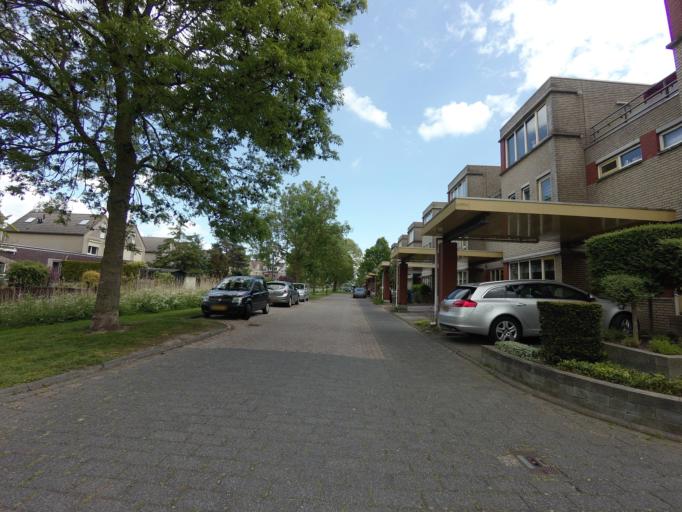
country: NL
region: North Brabant
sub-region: Gemeente Woudrichem
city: Woudrichem
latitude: 51.8379
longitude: 5.0001
